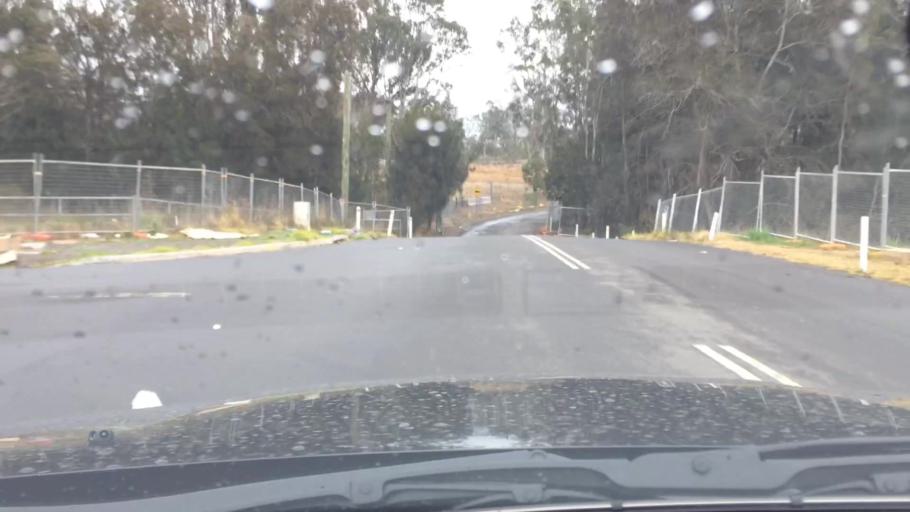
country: AU
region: New South Wales
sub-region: Campbelltown Municipality
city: Denham Court
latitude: -33.9609
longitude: 150.8460
